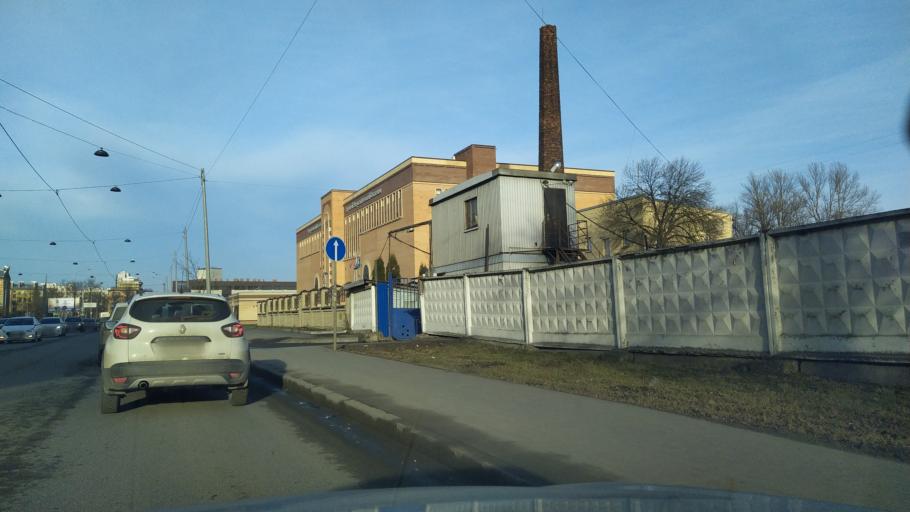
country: RU
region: St.-Petersburg
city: Centralniy
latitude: 59.9118
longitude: 30.3585
